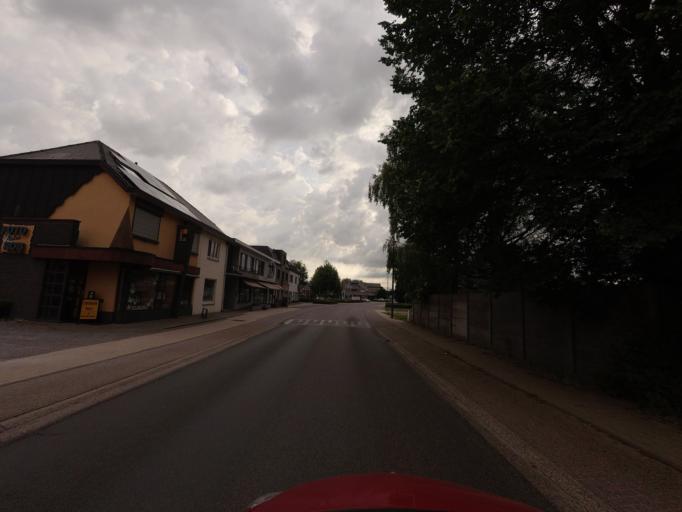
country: BE
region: Flanders
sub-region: Provincie Limburg
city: Lommel
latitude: 51.2319
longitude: 5.3308
